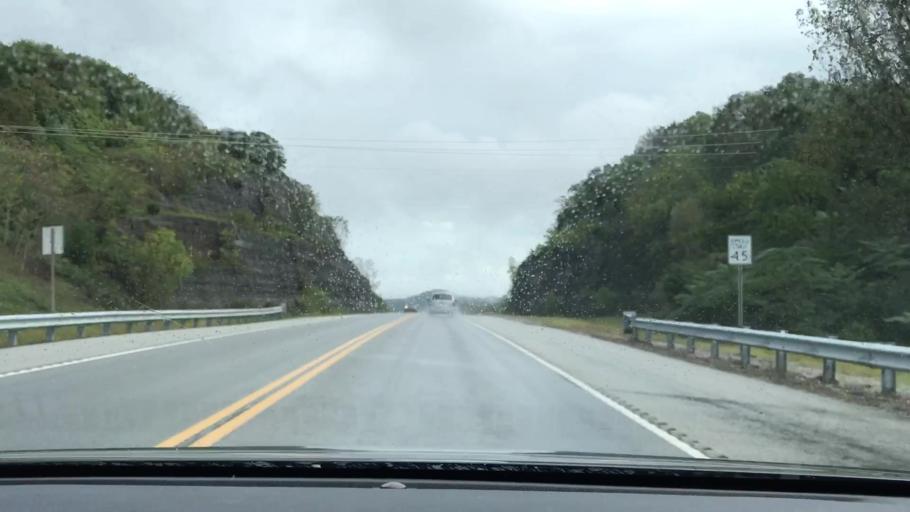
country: US
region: Tennessee
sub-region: Smith County
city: Carthage
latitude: 36.2611
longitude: -85.9431
